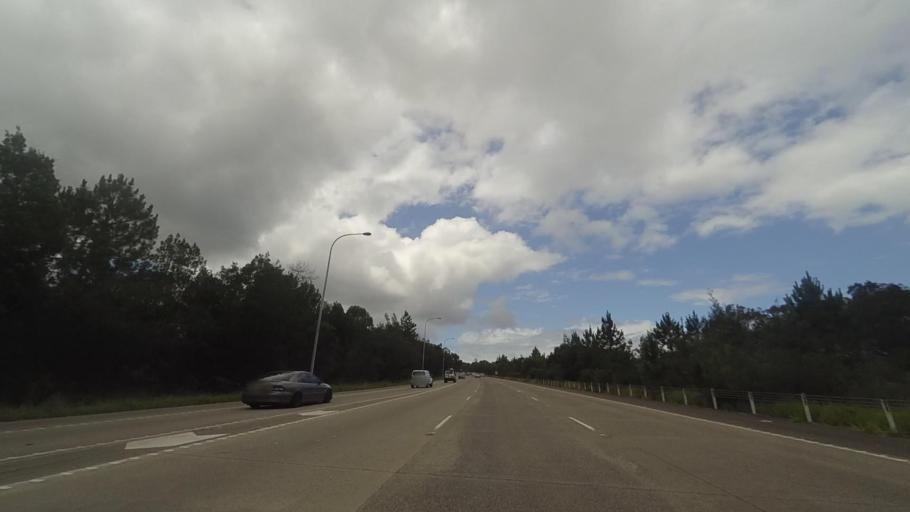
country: AU
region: New South Wales
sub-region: Gosford Shire
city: Point Clare
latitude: -33.4196
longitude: 151.2924
